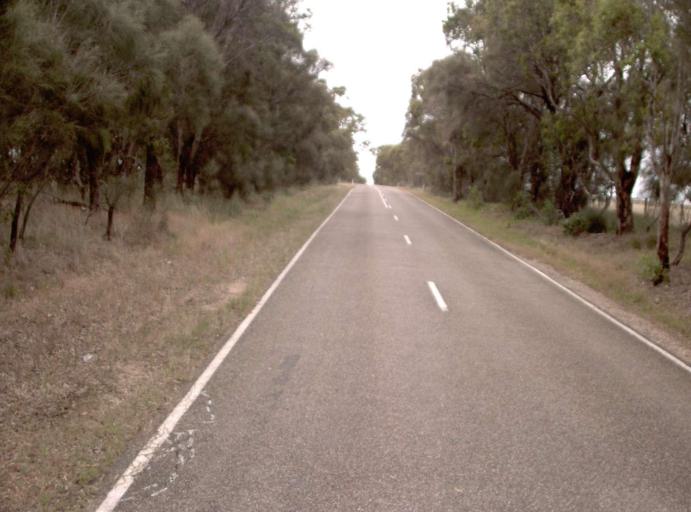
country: AU
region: Victoria
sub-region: Wellington
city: Sale
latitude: -37.9629
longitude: 147.1264
